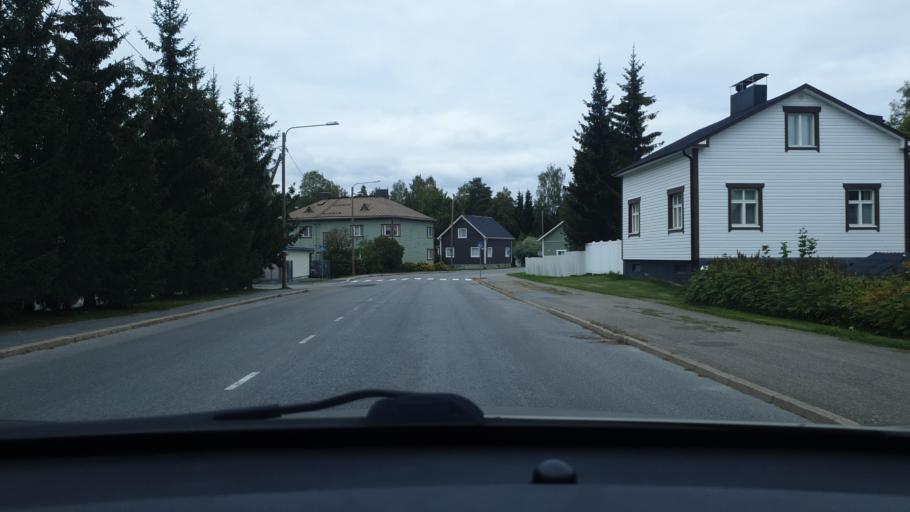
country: FI
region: Ostrobothnia
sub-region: Vaasa
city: Korsholm
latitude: 63.0935
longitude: 21.6654
